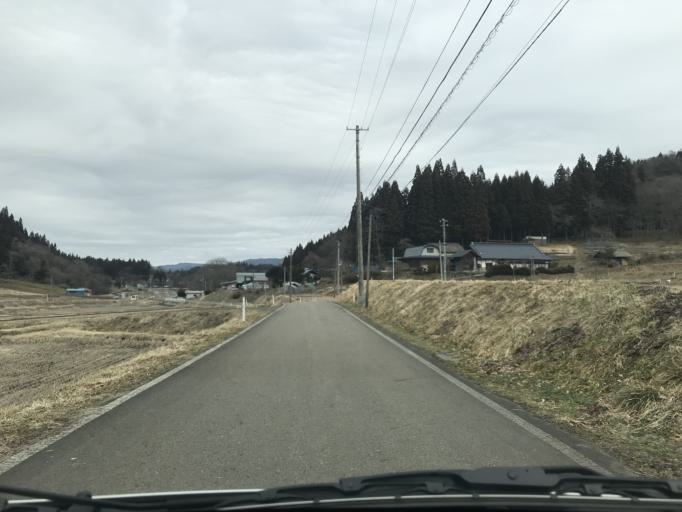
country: JP
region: Iwate
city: Kitakami
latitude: 39.3255
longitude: 141.2335
